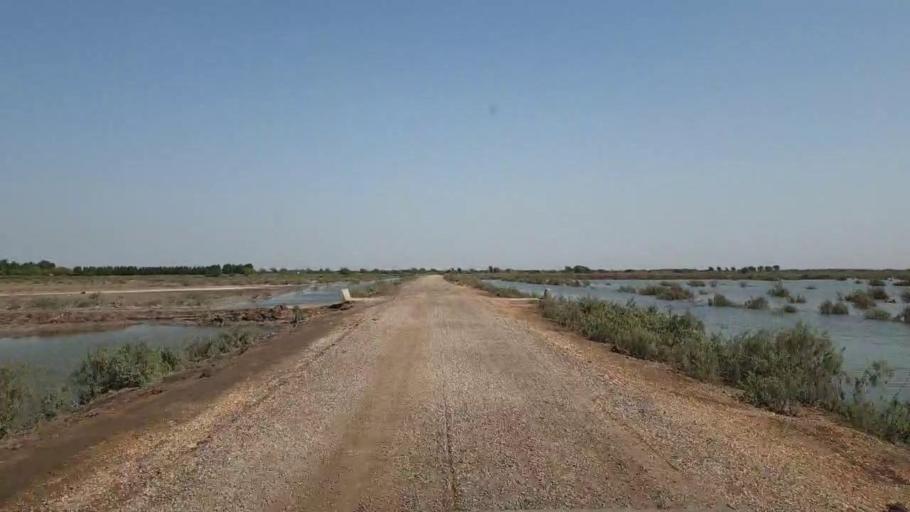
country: PK
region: Sindh
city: Tando Bago
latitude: 24.7303
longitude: 69.0361
